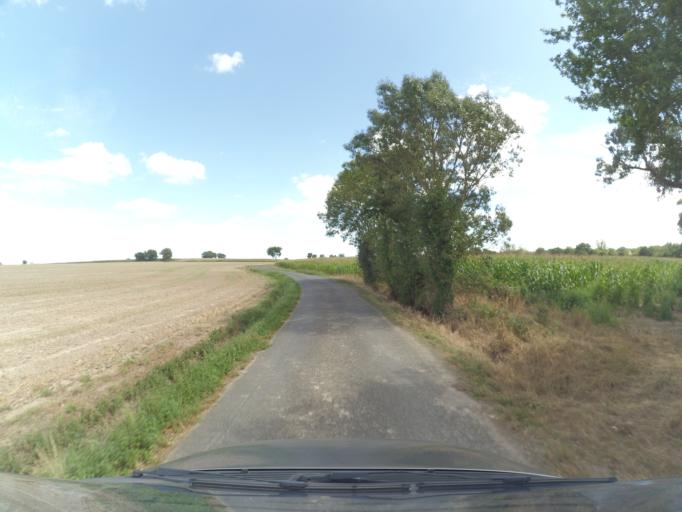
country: FR
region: Pays de la Loire
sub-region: Departement de la Loire-Atlantique
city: Saint-Hilaire-de-Clisson
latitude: 47.0472
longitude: -1.3386
